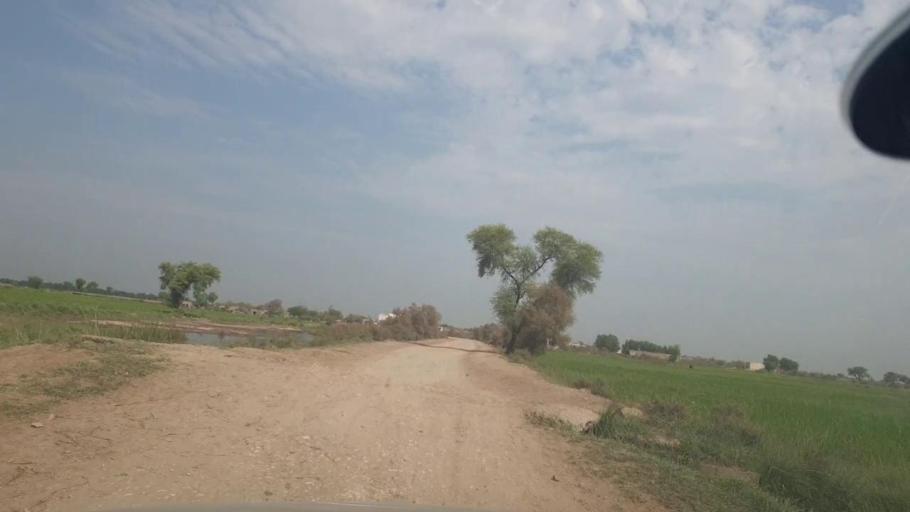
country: PK
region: Balochistan
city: Mehrabpur
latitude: 28.1259
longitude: 68.0894
